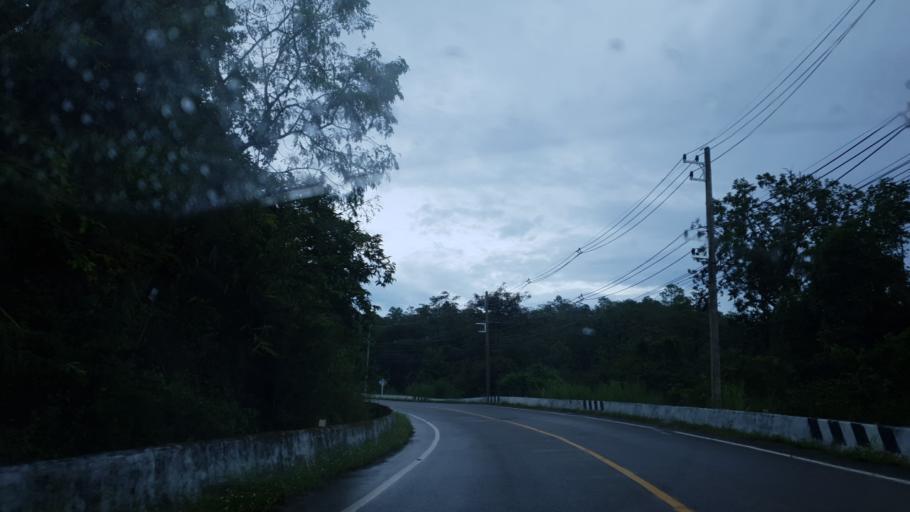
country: TH
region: Mae Hong Son
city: Ban Huai I Huak
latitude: 18.1426
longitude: 98.2029
